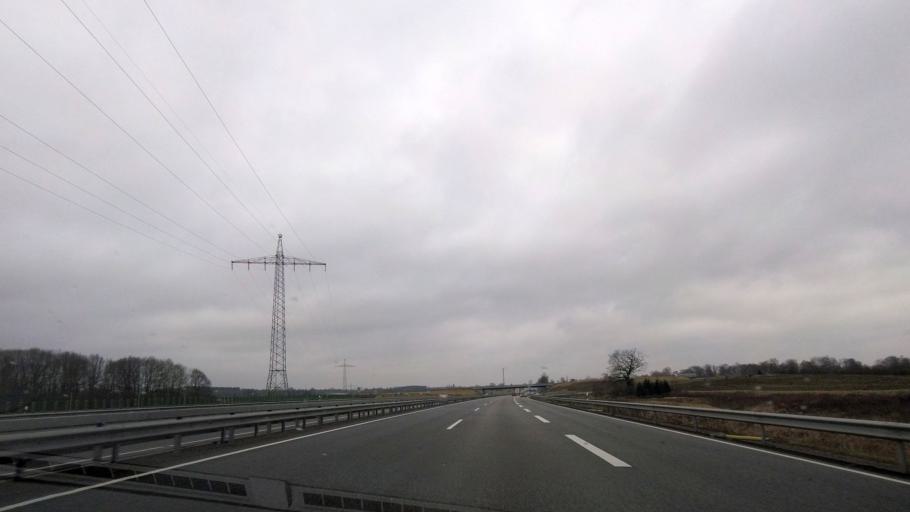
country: DE
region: Schleswig-Holstein
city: Loptin
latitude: 54.1610
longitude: 10.2033
